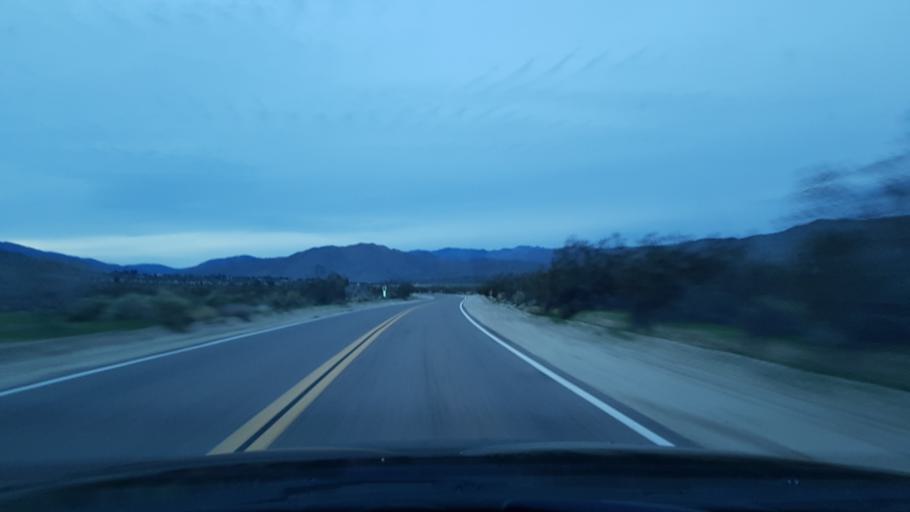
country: US
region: California
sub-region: San Diego County
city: Julian
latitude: 33.0483
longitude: -116.4152
